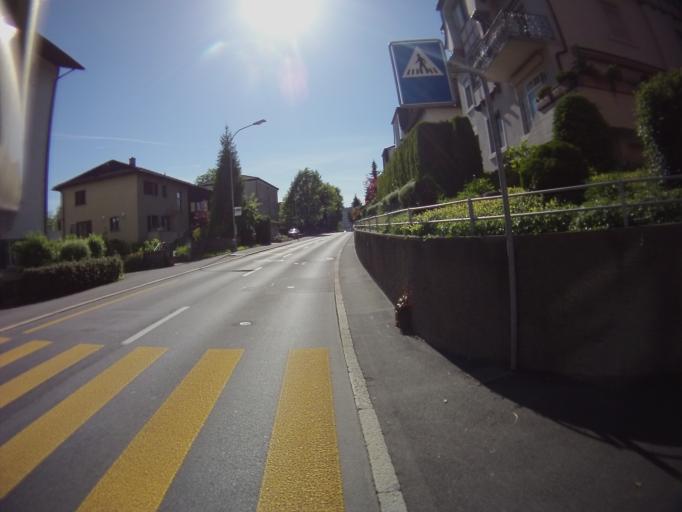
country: CH
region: Zug
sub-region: Zug
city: Cham
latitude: 47.1796
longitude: 8.4567
